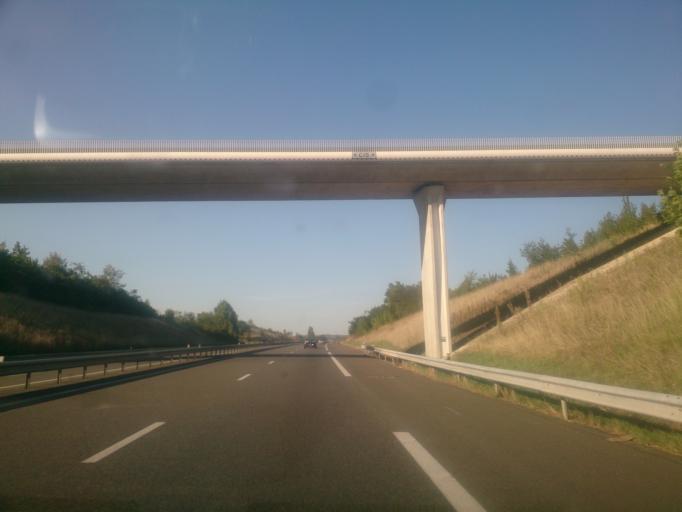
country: FR
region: Midi-Pyrenees
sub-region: Departement du Tarn-et-Garonne
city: Caussade
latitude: 44.1937
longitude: 1.5369
